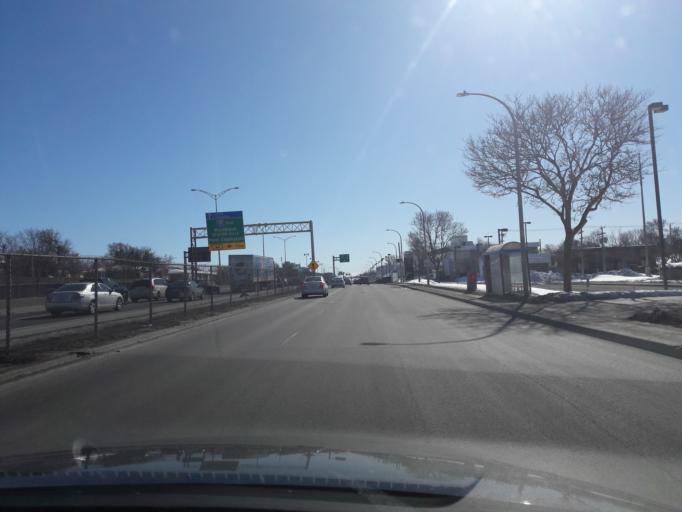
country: CA
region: Quebec
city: Mont-Royal
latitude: 45.5154
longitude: -73.6584
